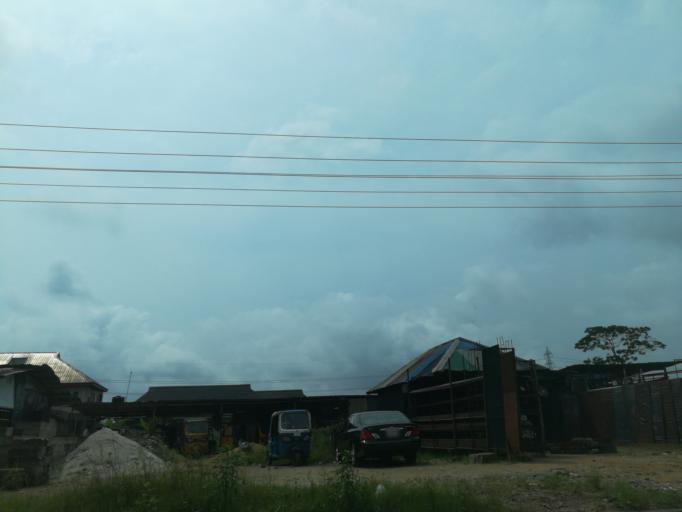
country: NG
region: Rivers
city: Port Harcourt
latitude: 4.8950
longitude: 6.9914
